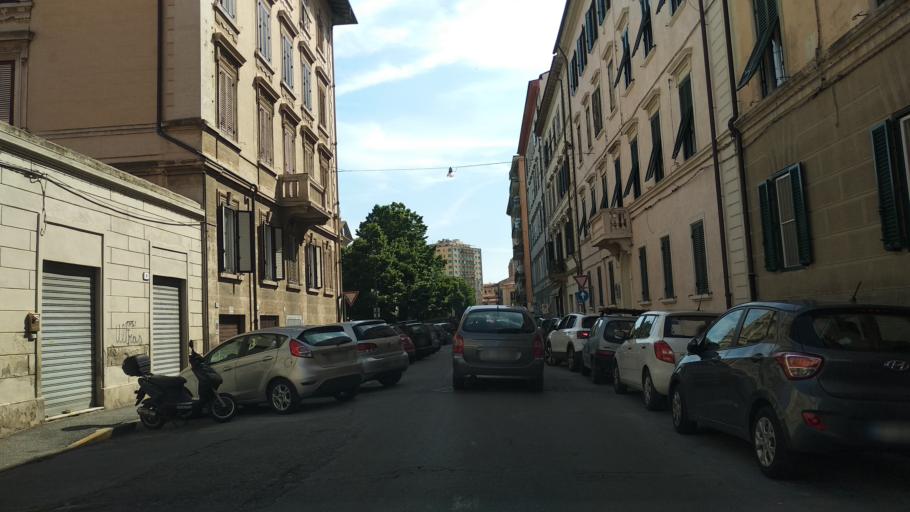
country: IT
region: Tuscany
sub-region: Provincia di Livorno
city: Livorno
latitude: 43.5473
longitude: 10.3171
